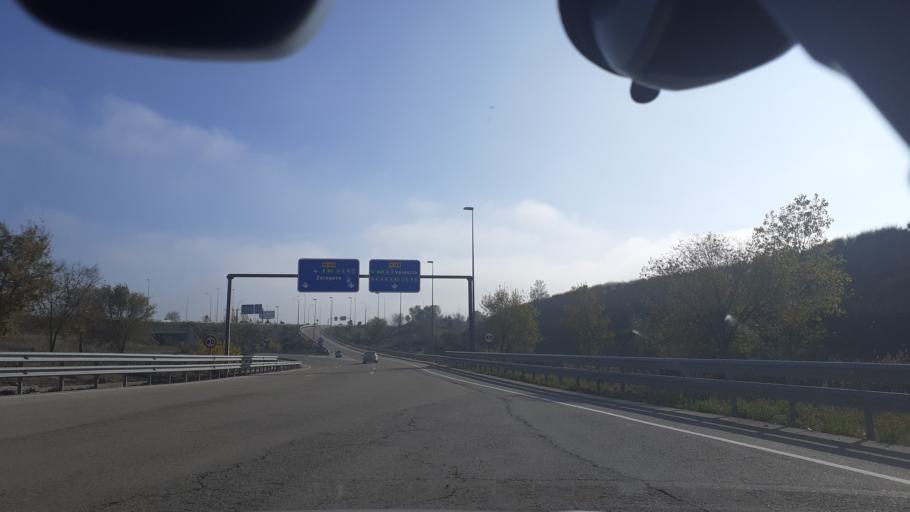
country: ES
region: Madrid
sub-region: Provincia de Madrid
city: Vicalvaro
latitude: 40.4018
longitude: -3.5768
